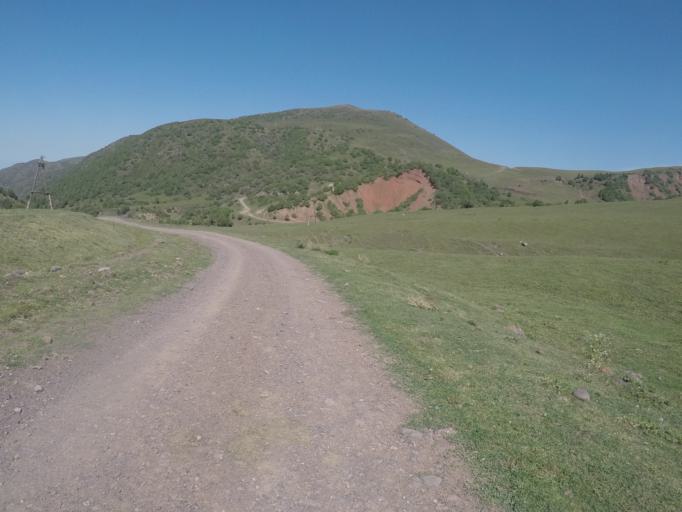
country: KG
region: Chuy
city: Bishkek
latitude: 42.6448
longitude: 74.5739
